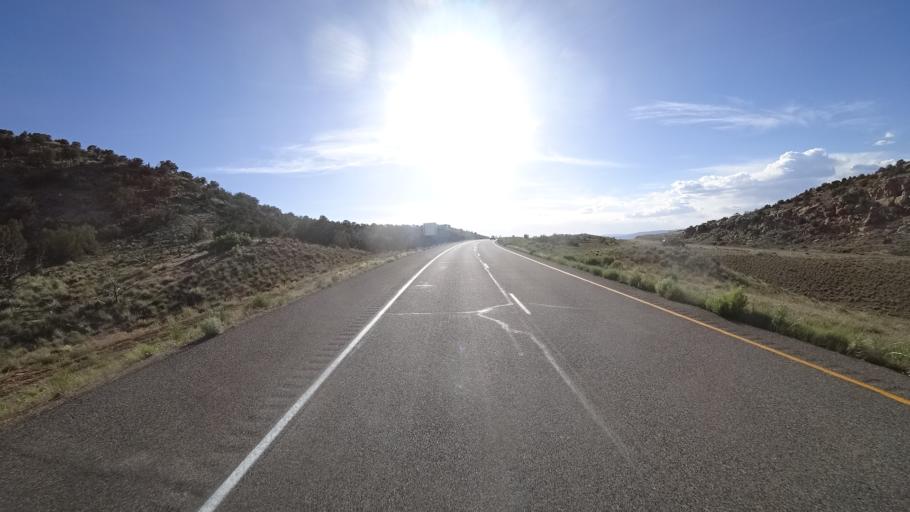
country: US
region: Colorado
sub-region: Mesa County
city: Loma
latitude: 39.1874
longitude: -109.0344
